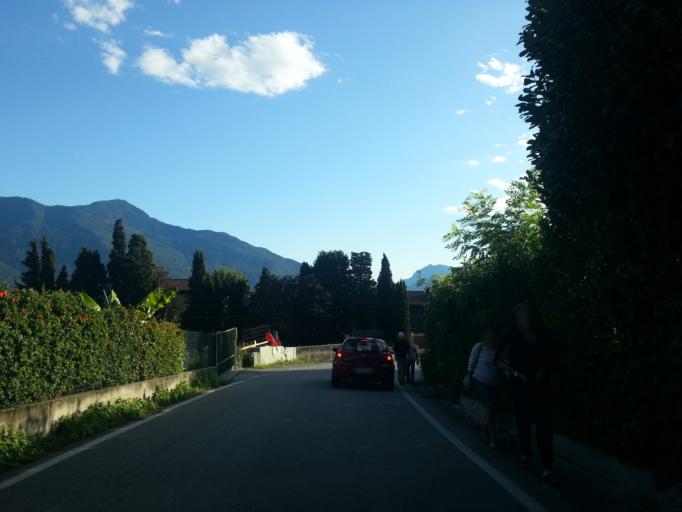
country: IT
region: Lombardy
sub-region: Provincia di Como
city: Gera Lario
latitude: 46.1695
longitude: 9.3676
